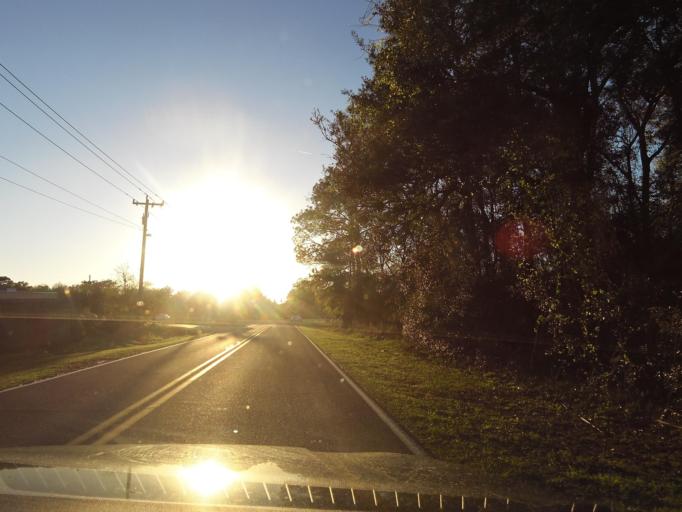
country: US
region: Florida
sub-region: Alachua County
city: Waldo
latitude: 29.8642
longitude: -82.1517
